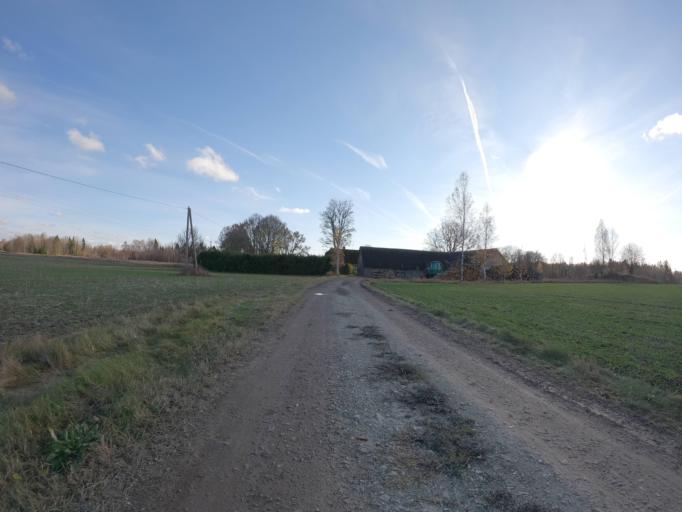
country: EE
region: Raplamaa
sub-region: Rapla vald
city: Rapla
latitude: 59.0255
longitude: 24.7944
